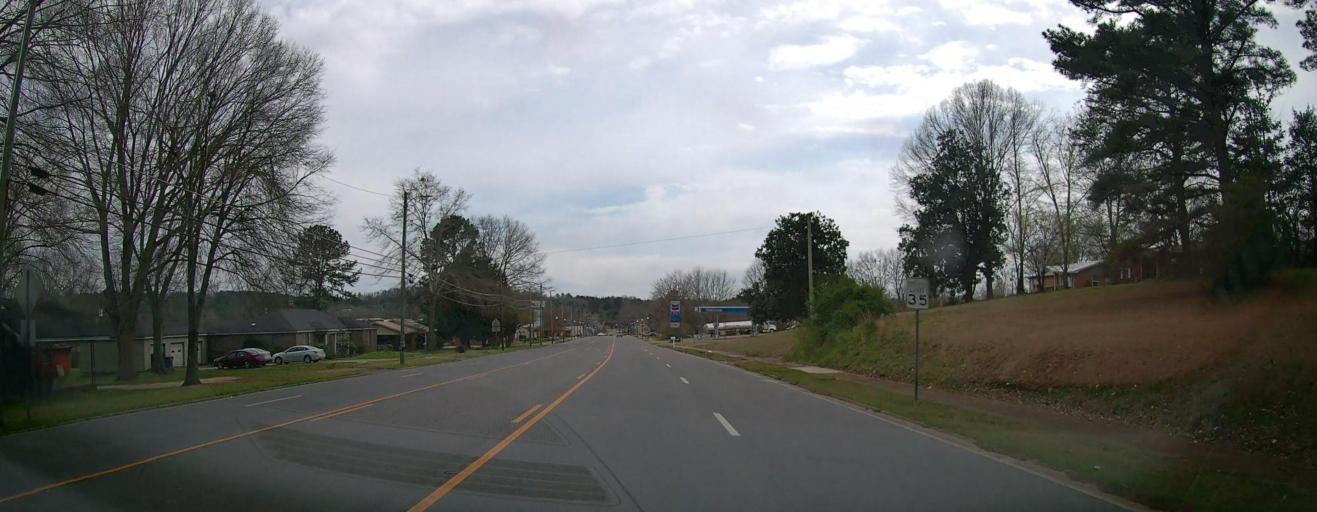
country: US
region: Alabama
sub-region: Marion County
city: Guin
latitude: 33.9694
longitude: -87.9153
